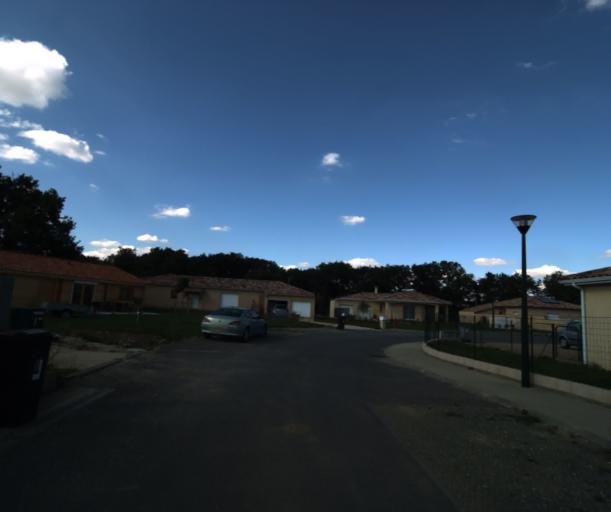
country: FR
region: Midi-Pyrenees
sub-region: Departement de la Haute-Garonne
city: Saint-Lys
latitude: 43.4994
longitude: 1.1919
